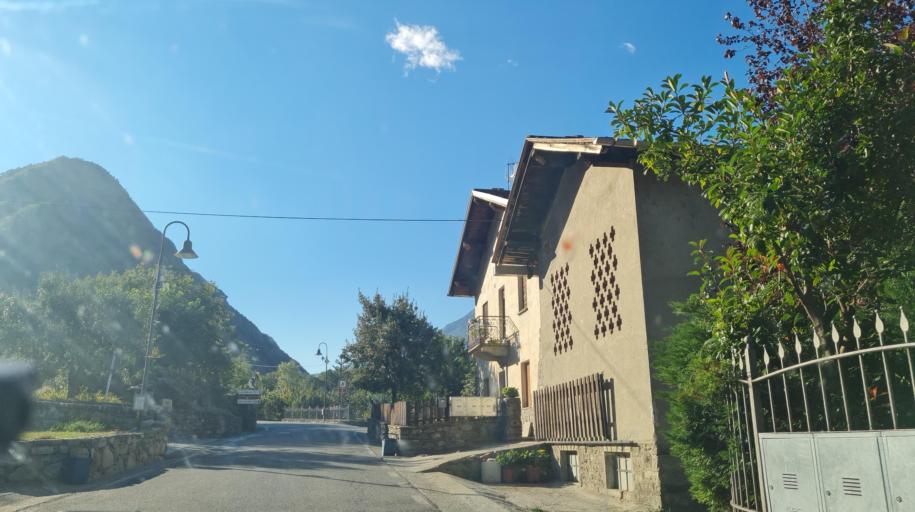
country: IT
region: Aosta Valley
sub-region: Valle d'Aosta
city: Arnad
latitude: 45.6410
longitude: 7.7244
